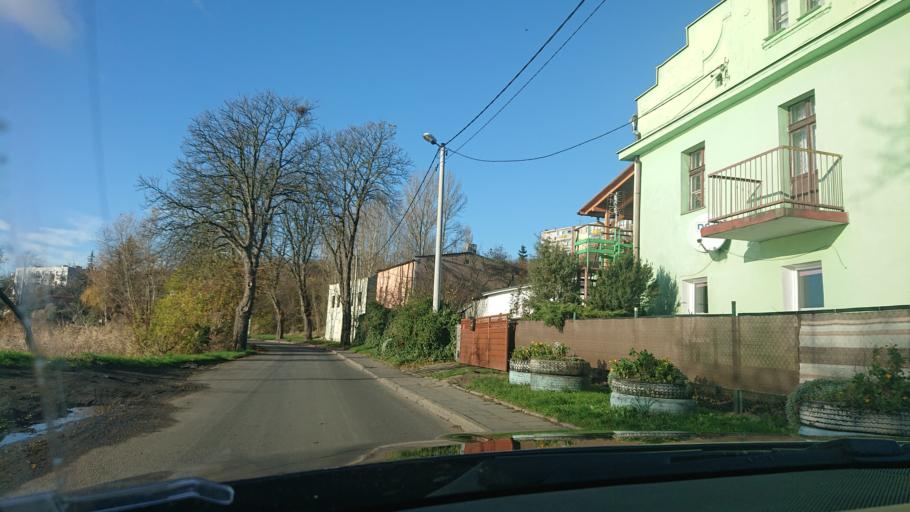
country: PL
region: Greater Poland Voivodeship
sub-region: Powiat gnieznienski
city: Gniezno
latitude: 52.5452
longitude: 17.5997
